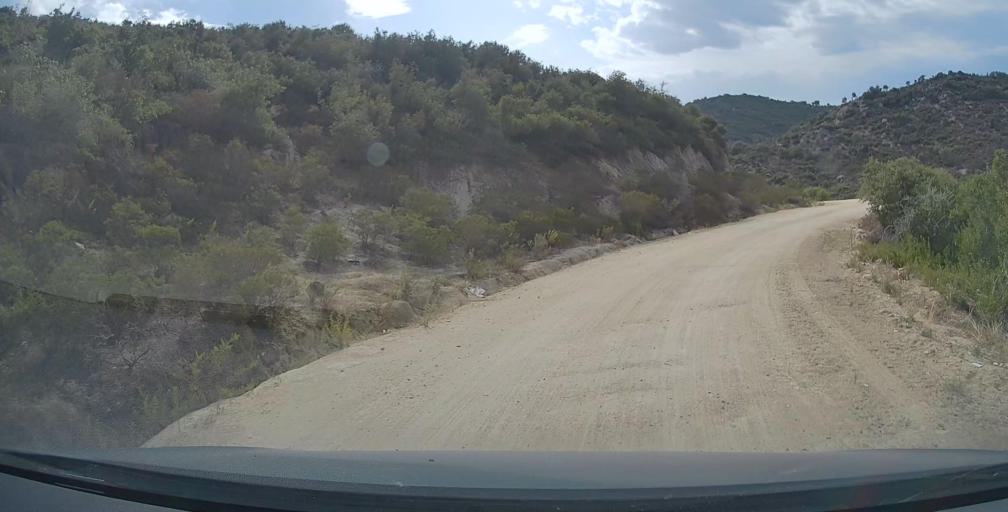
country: GR
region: Central Macedonia
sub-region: Nomos Chalkidikis
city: Sykia
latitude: 39.9896
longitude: 23.9149
